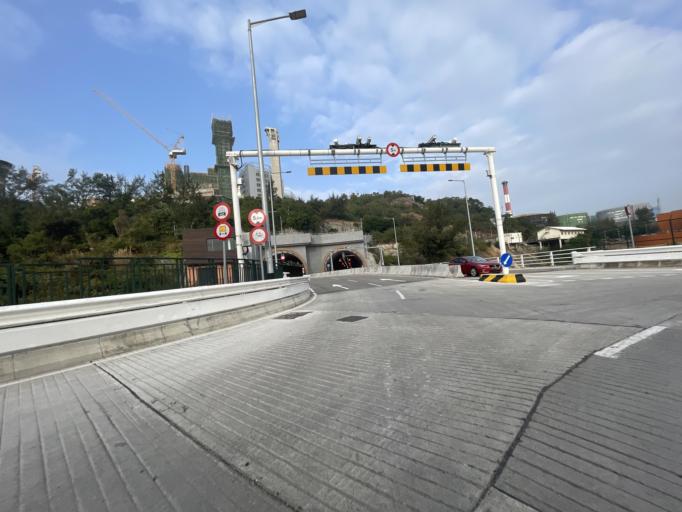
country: MO
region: Macau
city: Macau
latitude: 22.1353
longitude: 113.5800
